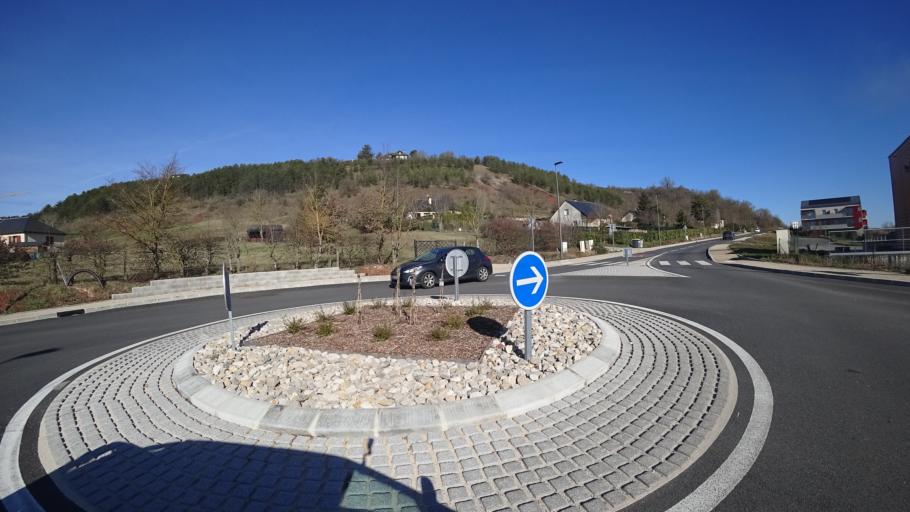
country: FR
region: Midi-Pyrenees
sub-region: Departement de l'Aveyron
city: Rodez
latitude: 44.3767
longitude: 2.5795
